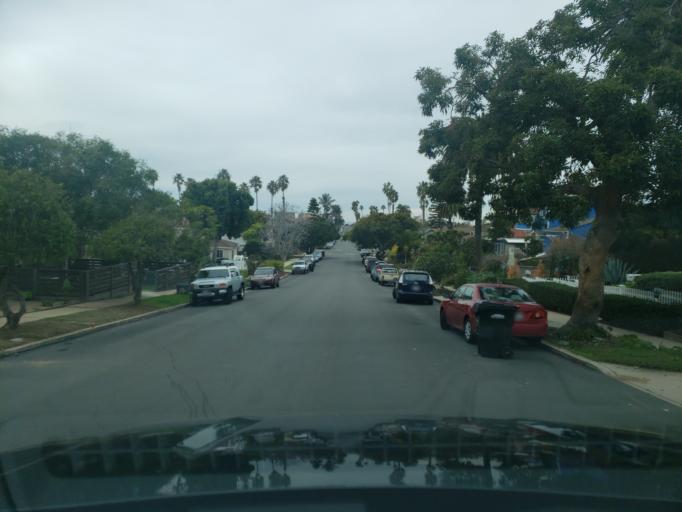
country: US
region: California
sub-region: San Diego County
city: Coronado
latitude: 32.7389
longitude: -117.2507
